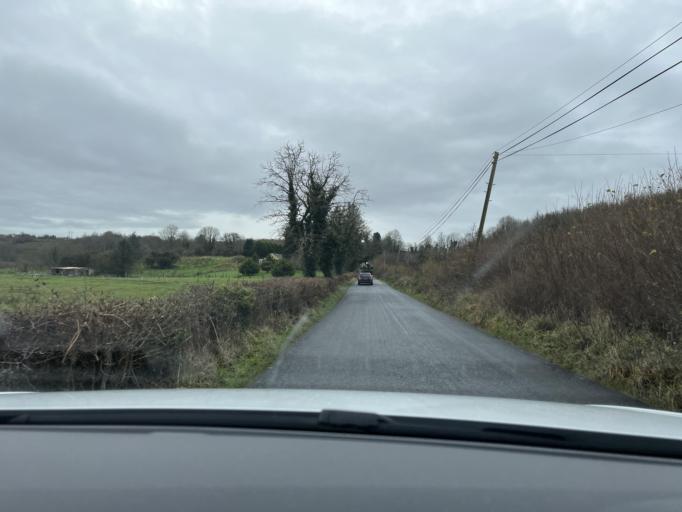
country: IE
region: Connaught
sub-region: County Leitrim
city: Manorhamilton
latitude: 54.2384
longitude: -8.2730
